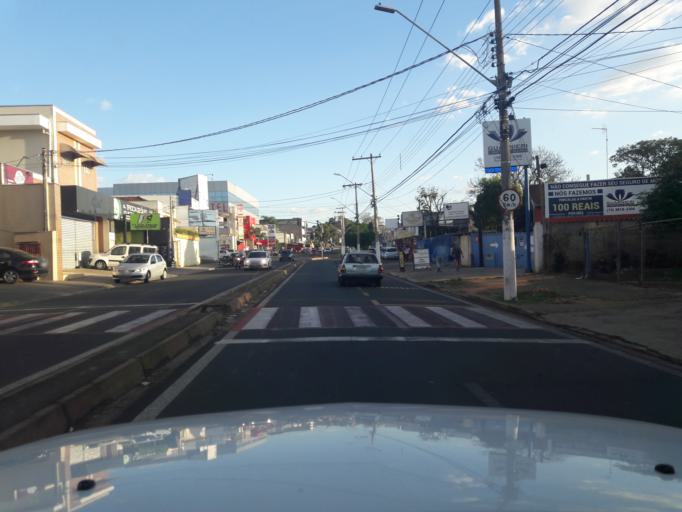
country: BR
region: Sao Paulo
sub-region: Moji-Guacu
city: Mogi-Gaucu
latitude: -22.3839
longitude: -46.9429
